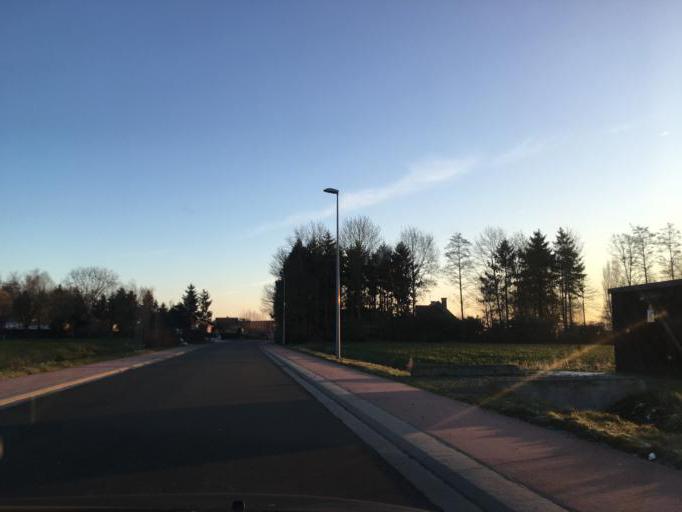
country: BE
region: Flanders
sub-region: Provincie Oost-Vlaanderen
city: Zomergem
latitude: 51.1432
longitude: 3.5627
